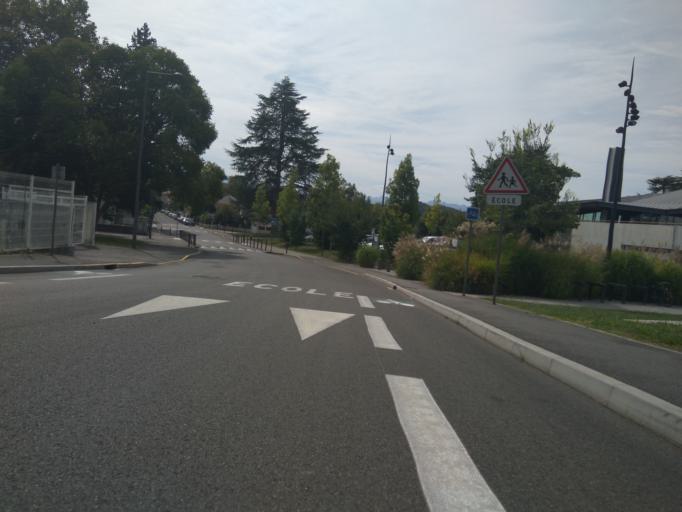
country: FR
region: Aquitaine
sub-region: Departement des Pyrenees-Atlantiques
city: Bizanos
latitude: 43.2955
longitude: -0.3540
